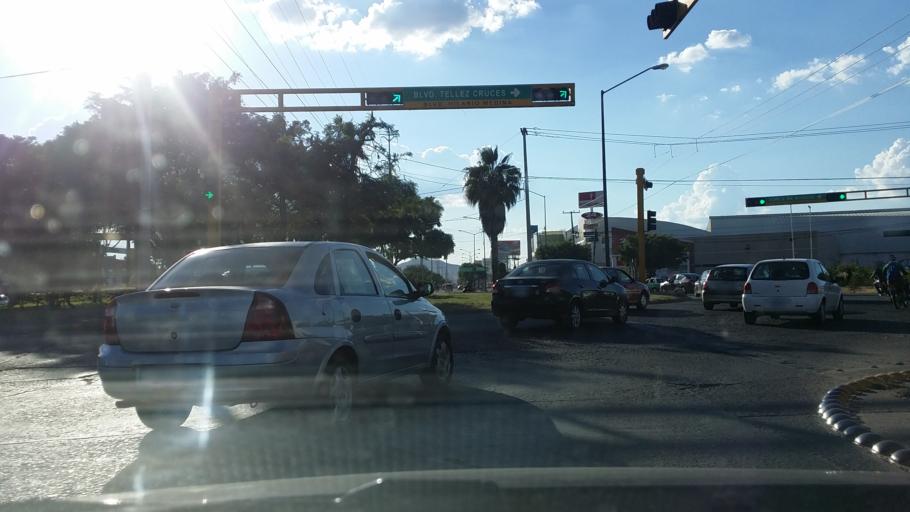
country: MX
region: Guanajuato
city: Leon
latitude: 21.1464
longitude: -101.6509
